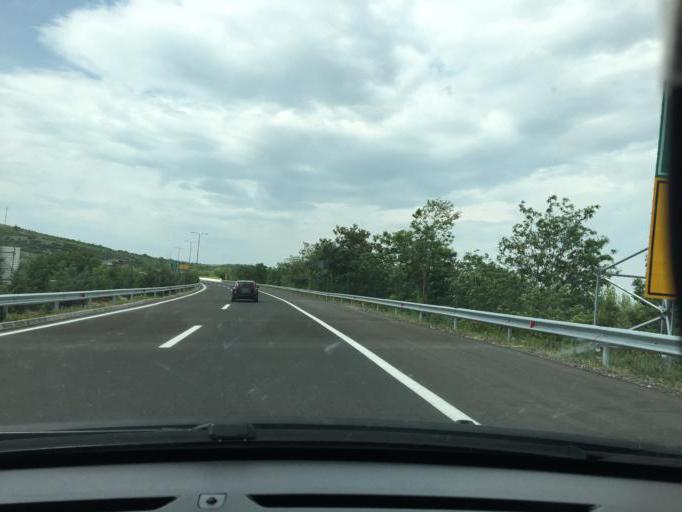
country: MK
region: Demir Kapija
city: Demir Kapija
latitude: 41.4156
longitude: 22.2396
